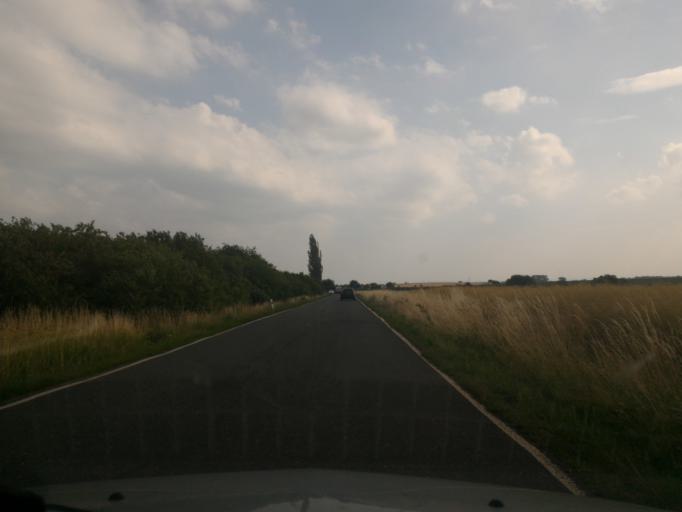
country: CZ
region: Central Bohemia
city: Loucen
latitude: 50.2583
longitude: 15.0250
